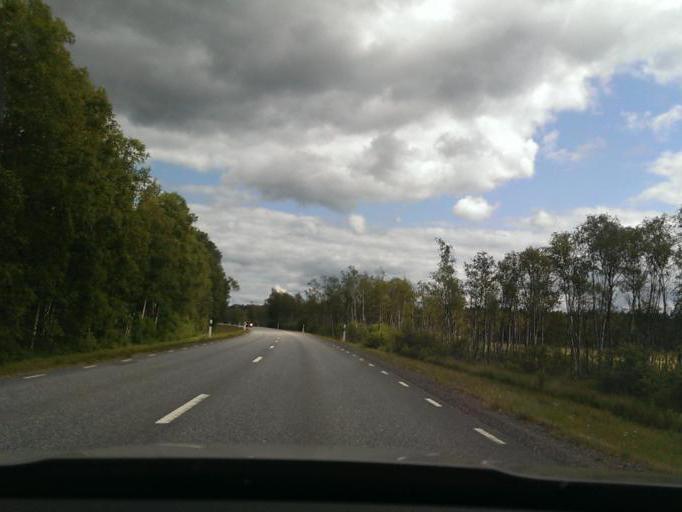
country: SE
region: Joenkoeping
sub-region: Gnosjo Kommun
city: Hillerstorp
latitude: 57.2913
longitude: 13.9379
